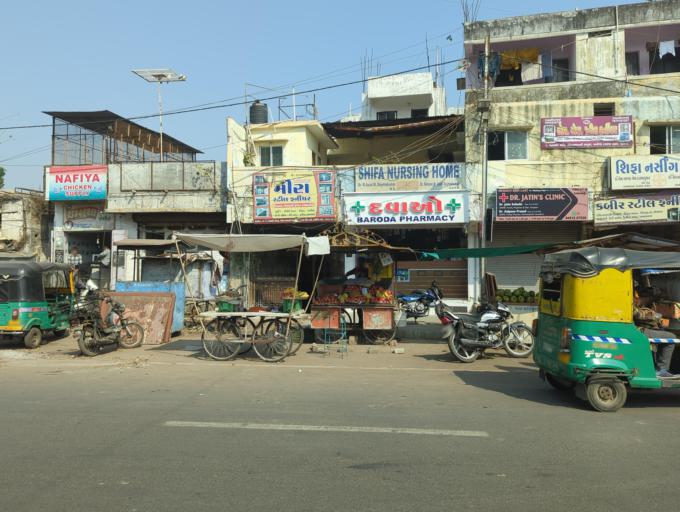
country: IN
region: Gujarat
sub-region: Vadodara
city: Vadodara
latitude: 22.2991
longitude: 73.2172
